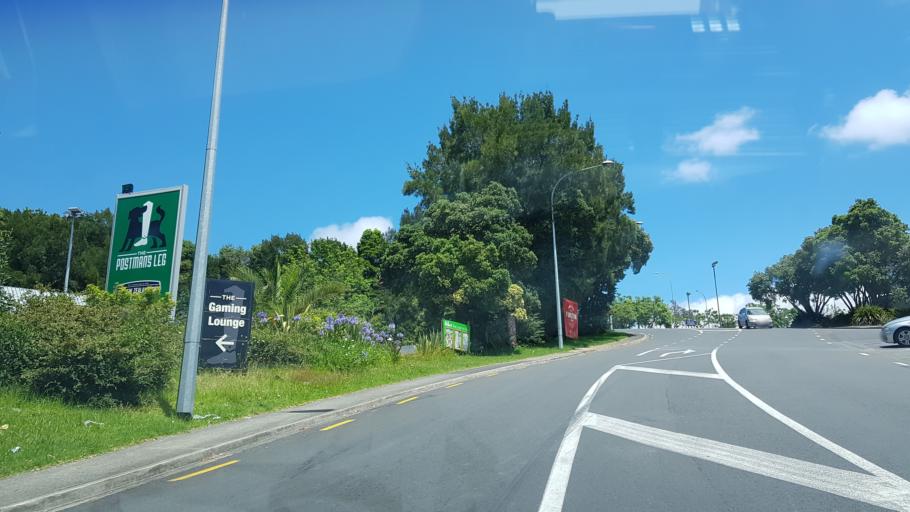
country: NZ
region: Auckland
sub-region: Auckland
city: North Shore
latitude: -36.7834
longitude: 174.7229
